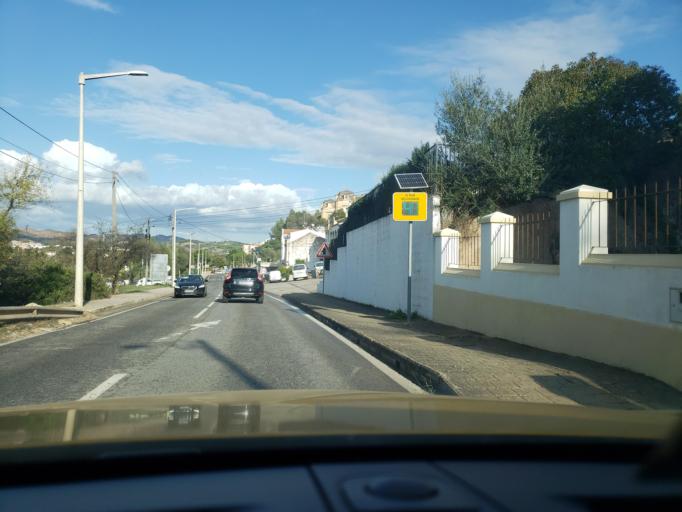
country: PT
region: Faro
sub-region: Silves
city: Silves
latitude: 37.1848
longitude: -8.4376
